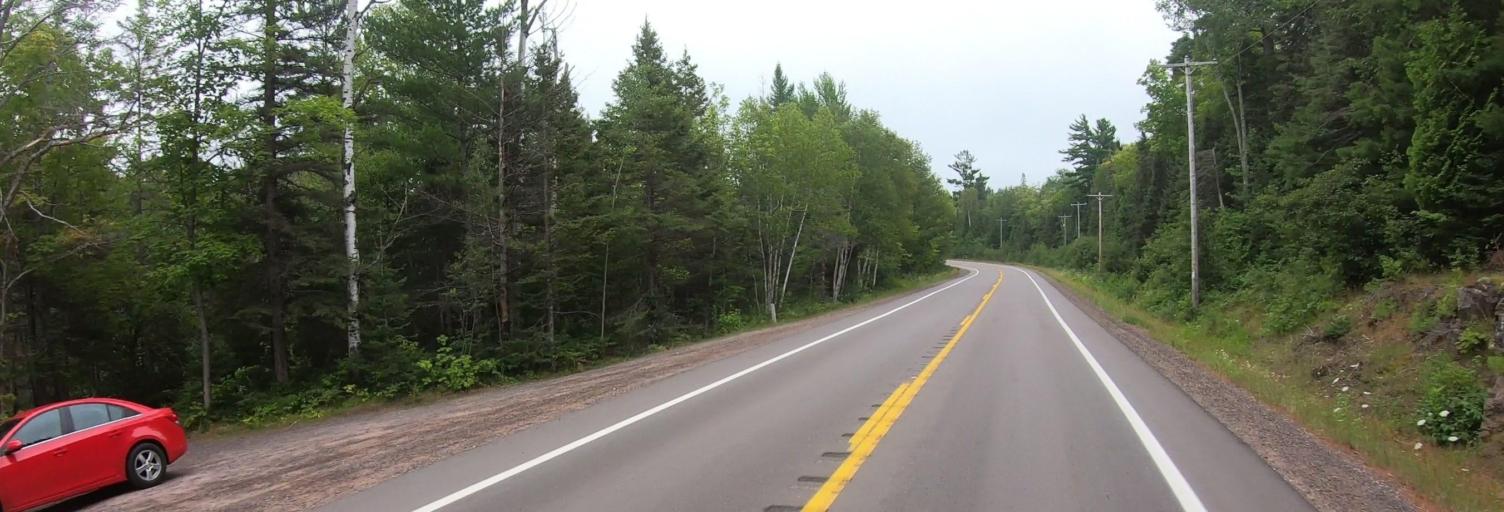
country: US
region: Michigan
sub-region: Keweenaw County
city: Eagle River
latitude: 47.3972
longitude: -88.2849
